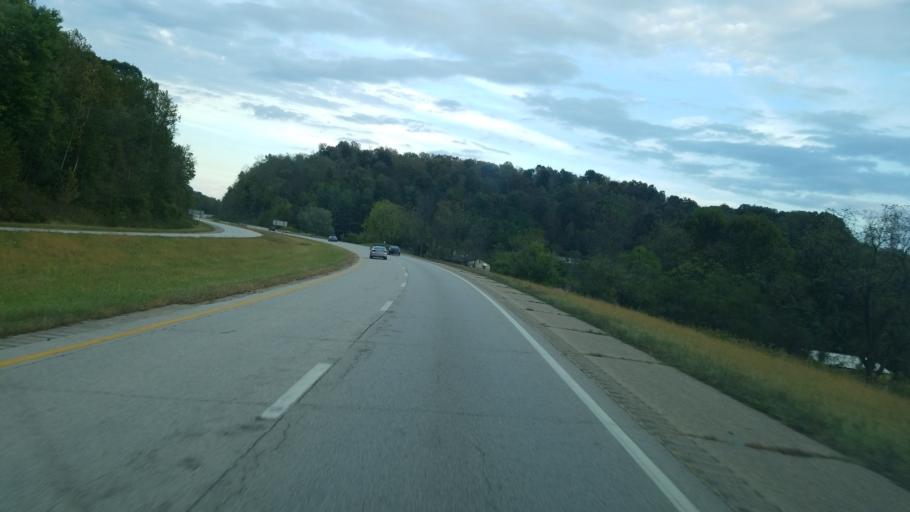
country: US
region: Ohio
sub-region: Meigs County
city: Pomeroy
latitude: 39.0476
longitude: -82.0462
